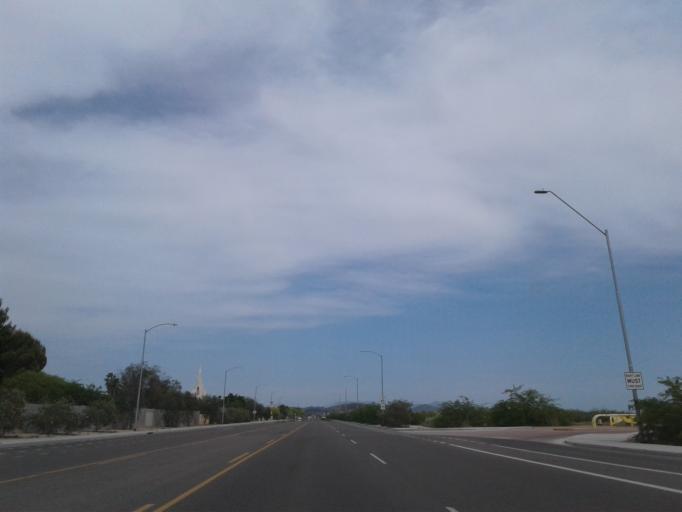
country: US
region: Arizona
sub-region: Maricopa County
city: Peoria
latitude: 33.6979
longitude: -112.1771
